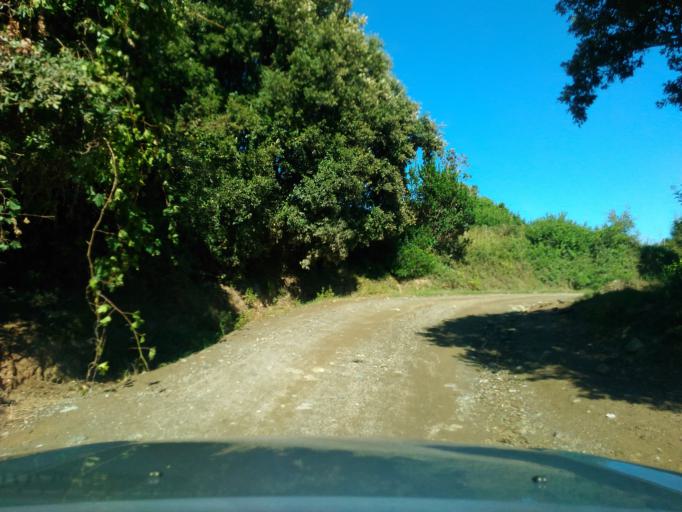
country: FR
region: Corsica
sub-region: Departement de la Haute-Corse
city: Brando
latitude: 42.9668
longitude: 9.4482
